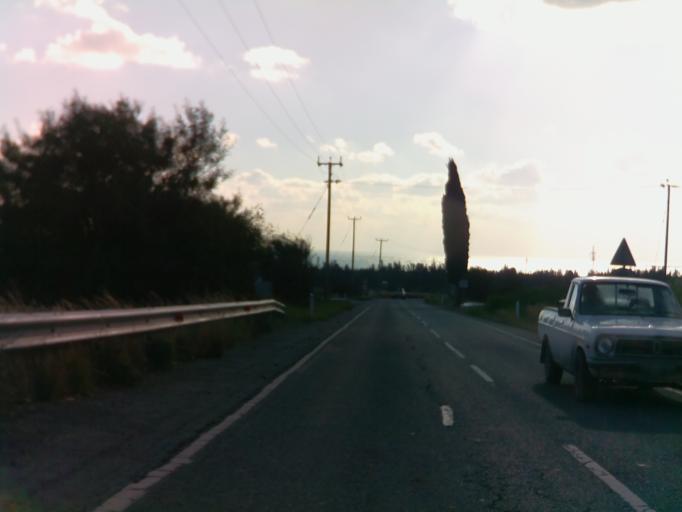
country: CY
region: Pafos
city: Mesogi
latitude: 34.7496
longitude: 32.5139
